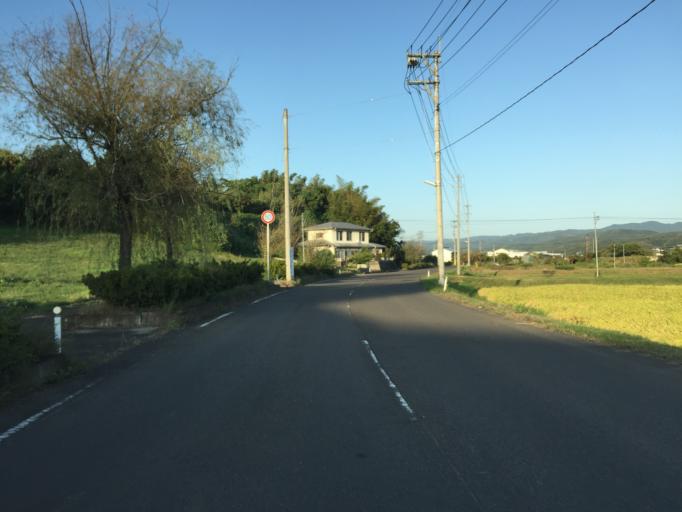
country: JP
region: Fukushima
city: Hobaramachi
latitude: 37.8040
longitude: 140.5485
